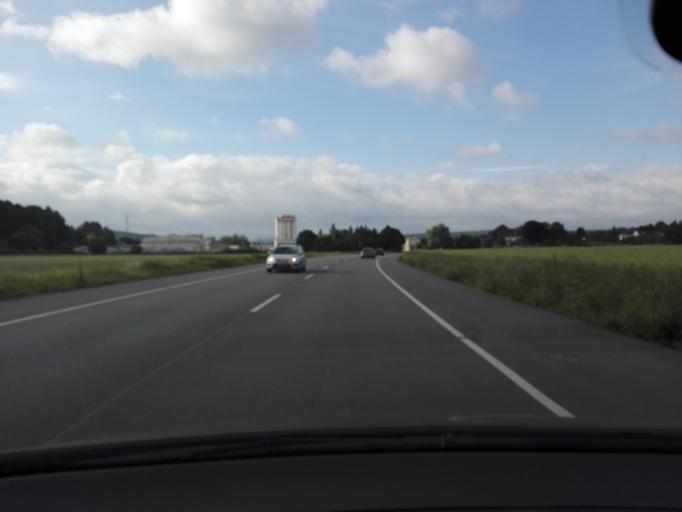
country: DE
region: North Rhine-Westphalia
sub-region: Regierungsbezirk Arnsberg
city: Frondenberg
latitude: 51.4634
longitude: 7.7750
